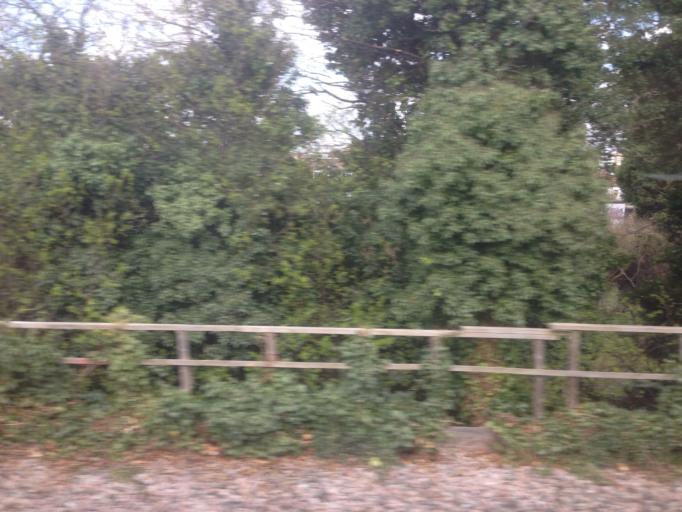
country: GB
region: England
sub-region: Greater London
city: Battersea
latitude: 51.4702
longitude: -0.1664
